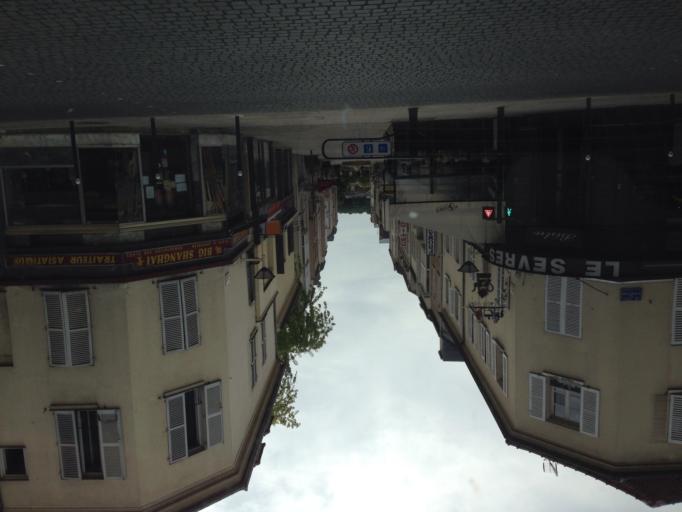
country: FR
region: Ile-de-France
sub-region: Departement des Hauts-de-Seine
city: Clamart
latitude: 48.8023
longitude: 2.2647
